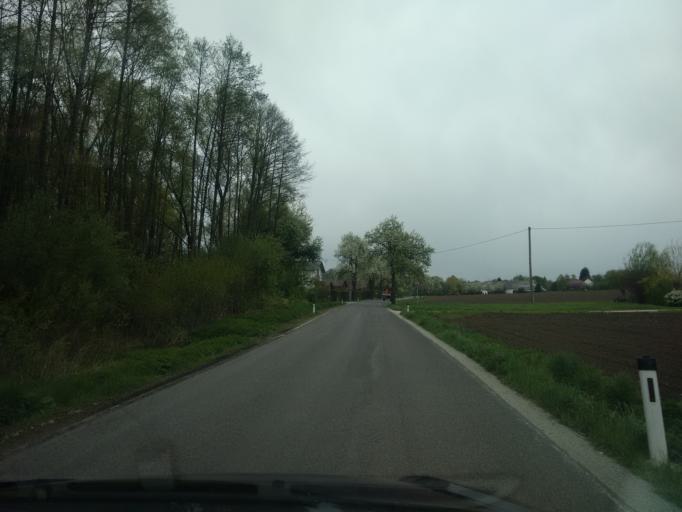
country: AT
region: Upper Austria
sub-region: Wels-Land
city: Buchkirchen
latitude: 48.2099
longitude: 13.9821
